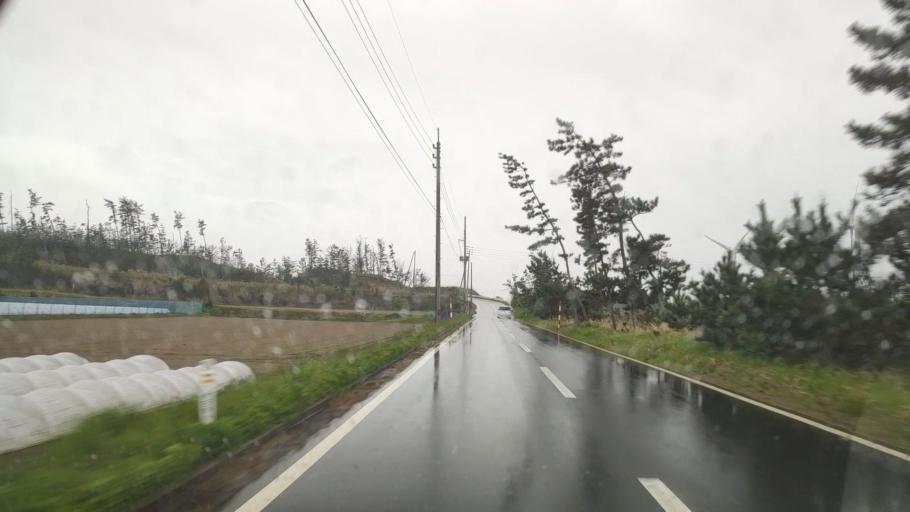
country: JP
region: Akita
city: Noshiromachi
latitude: 40.0778
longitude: 139.9527
